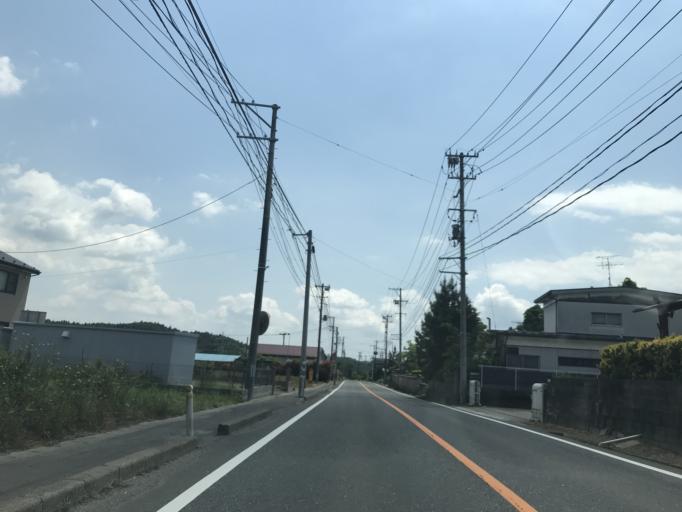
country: JP
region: Miyagi
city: Wakuya
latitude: 38.4885
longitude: 141.0900
